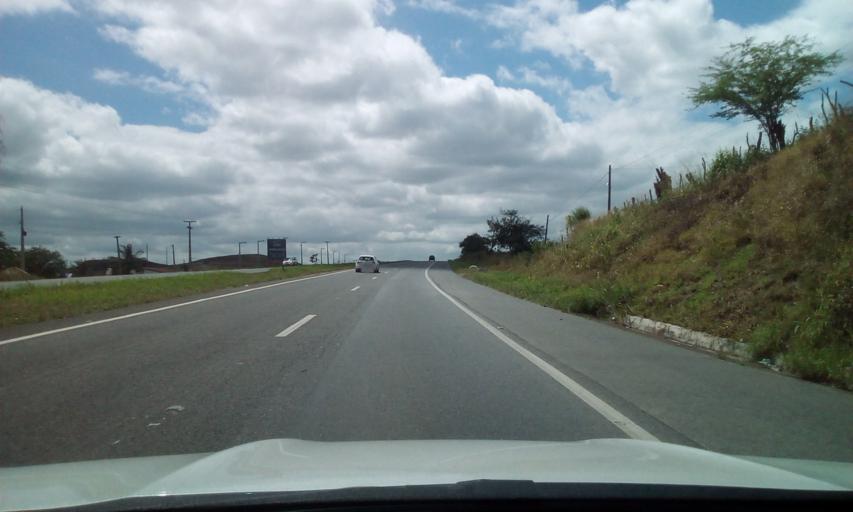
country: BR
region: Paraiba
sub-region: Massaranduba
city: Massaranduba
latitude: -7.2568
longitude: -35.8166
